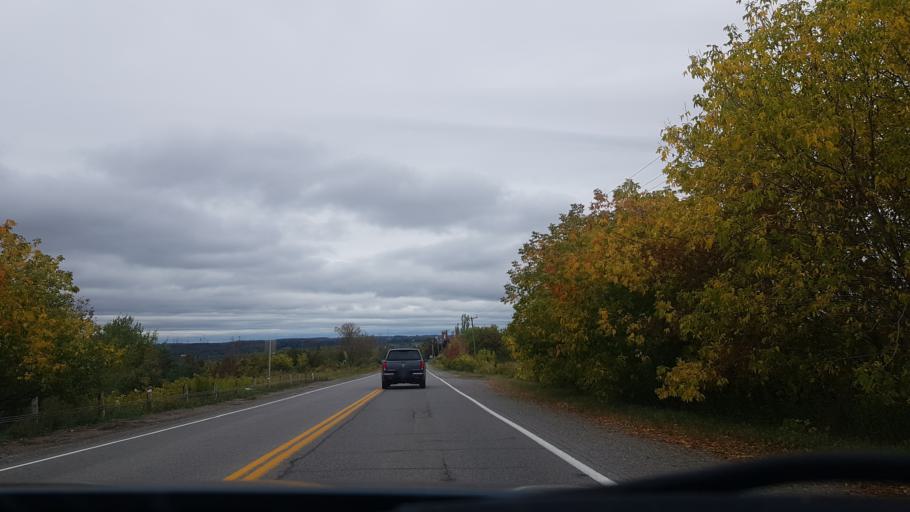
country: CA
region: Ontario
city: Omemee
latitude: 44.2191
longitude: -78.4771
